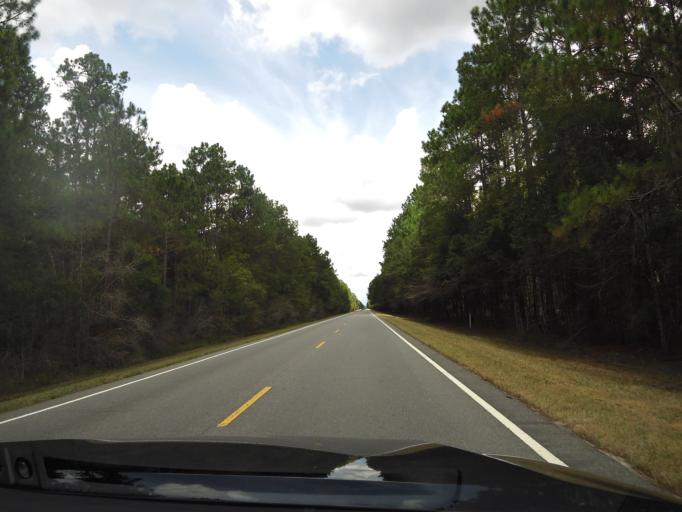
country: US
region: Georgia
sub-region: Charlton County
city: Folkston
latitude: 31.0111
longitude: -82.0261
